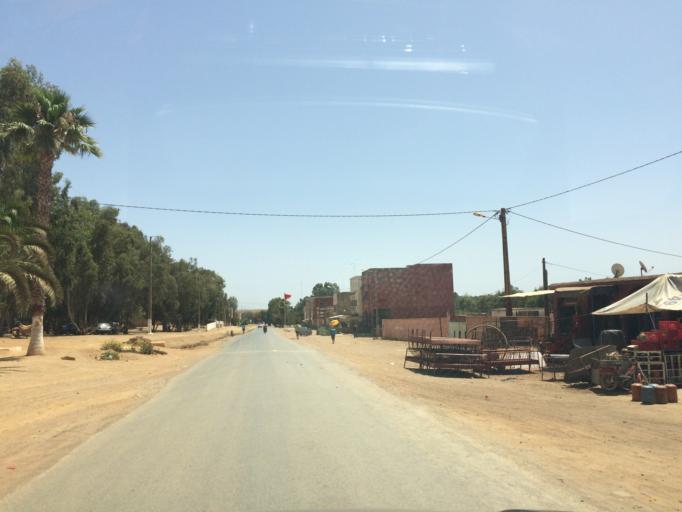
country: MA
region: Chaouia-Ouardigha
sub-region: Benslimane
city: Mellila
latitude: 33.5674
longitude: -6.8927
